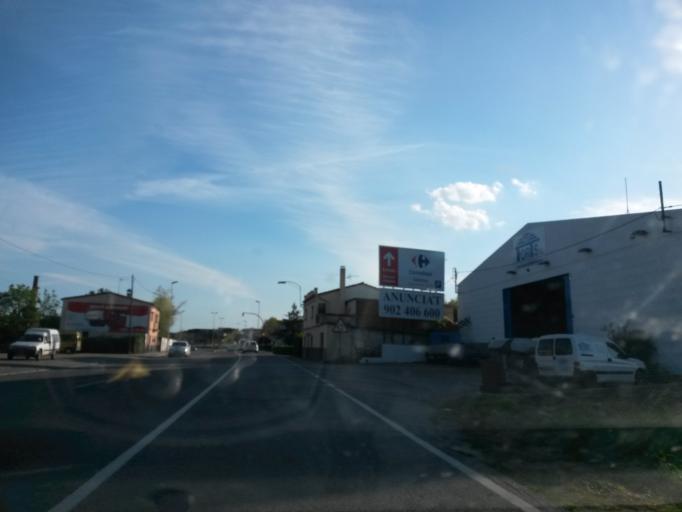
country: ES
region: Catalonia
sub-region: Provincia de Girona
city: Sarria de Ter
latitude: 42.0255
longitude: 2.8277
